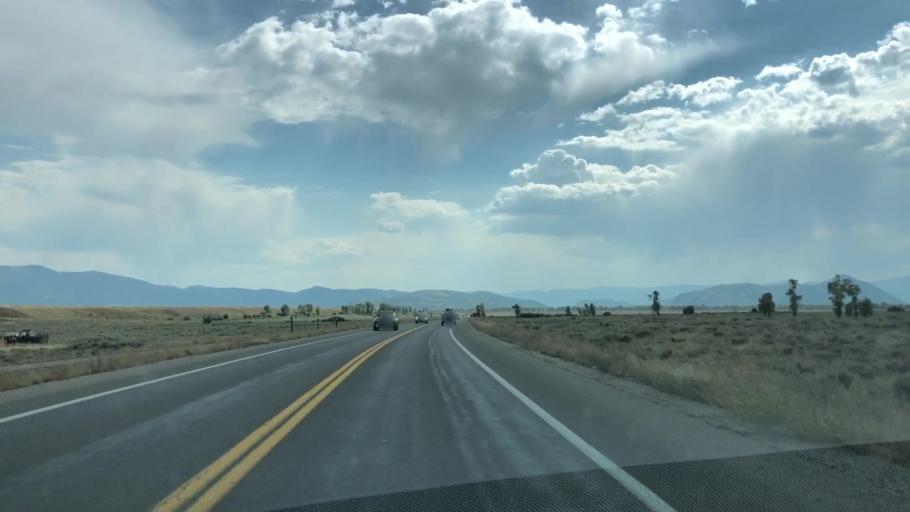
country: US
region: Wyoming
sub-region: Teton County
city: Jackson
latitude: 43.5969
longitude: -110.7251
